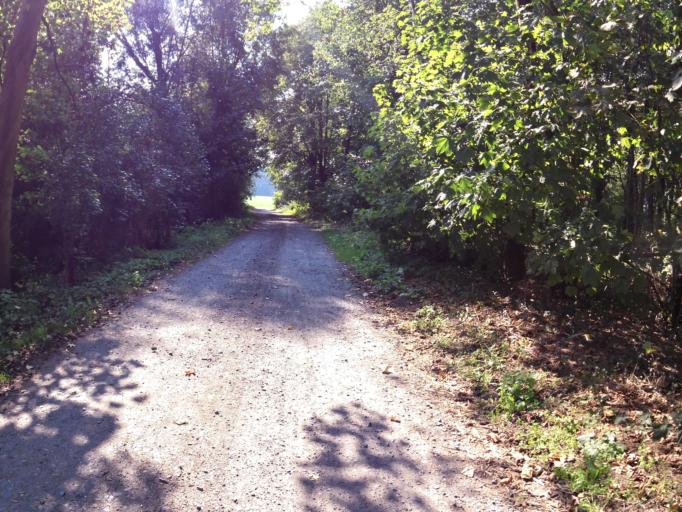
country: DE
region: North Rhine-Westphalia
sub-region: Regierungsbezirk Munster
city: Havixbeck
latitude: 51.9739
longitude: 7.4986
